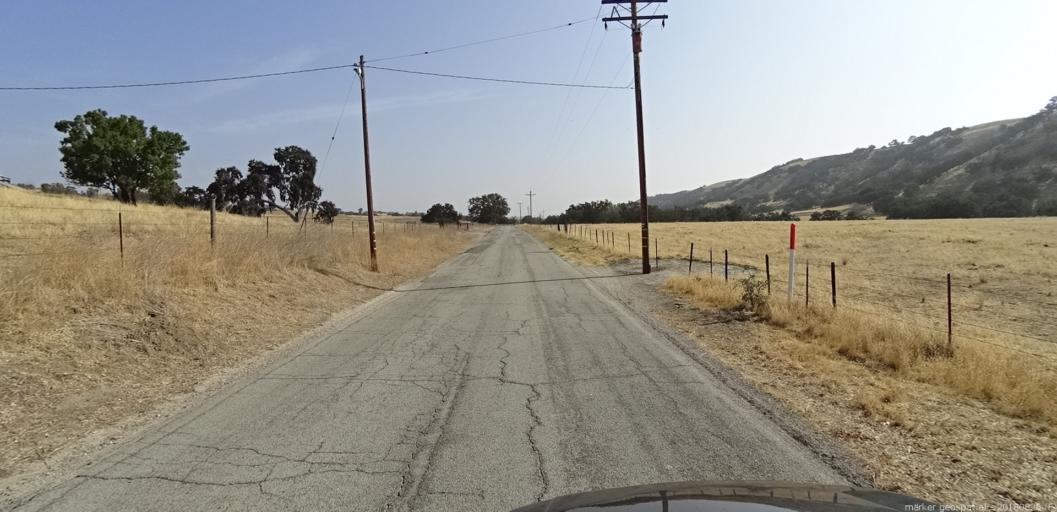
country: US
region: California
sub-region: San Luis Obispo County
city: San Miguel
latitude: 35.7699
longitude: -120.5984
